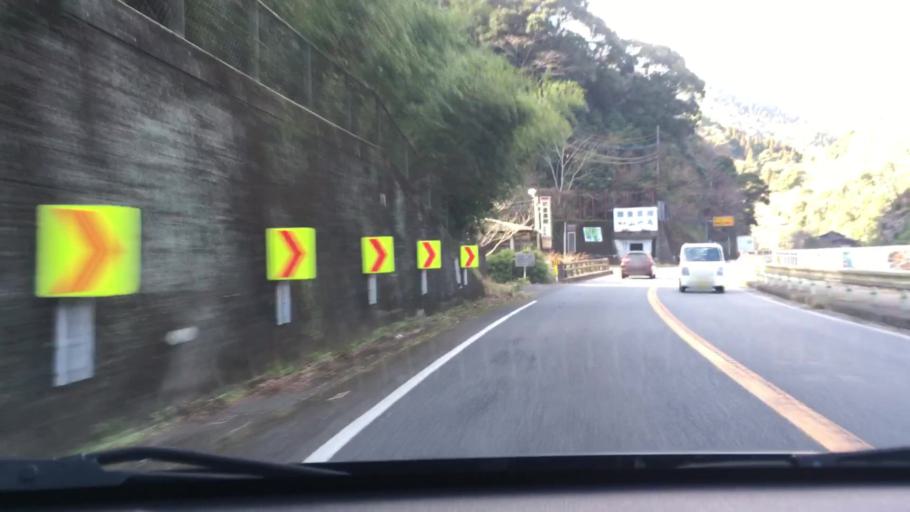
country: JP
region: Oita
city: Tsukumiura
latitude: 33.0034
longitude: 131.7991
